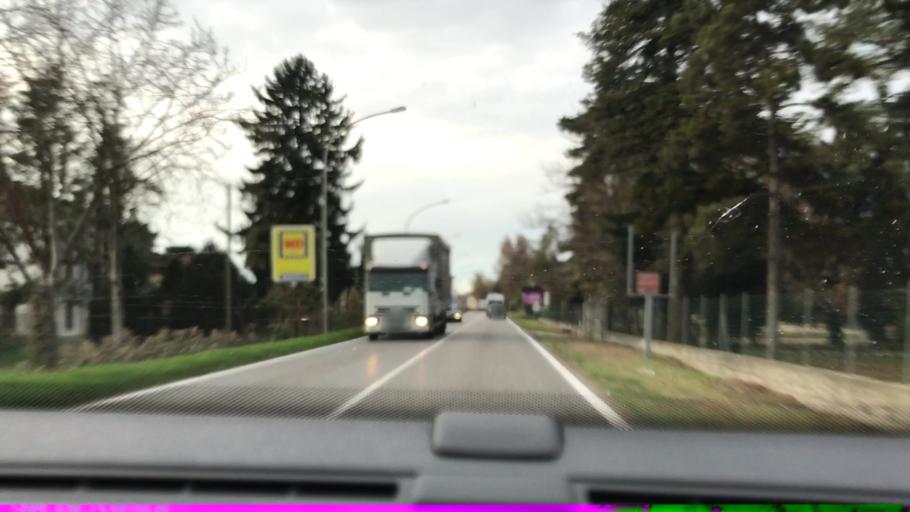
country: IT
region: Lombardy
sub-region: Provincia di Mantova
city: San Benedetto Po
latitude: 45.0370
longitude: 10.9307
